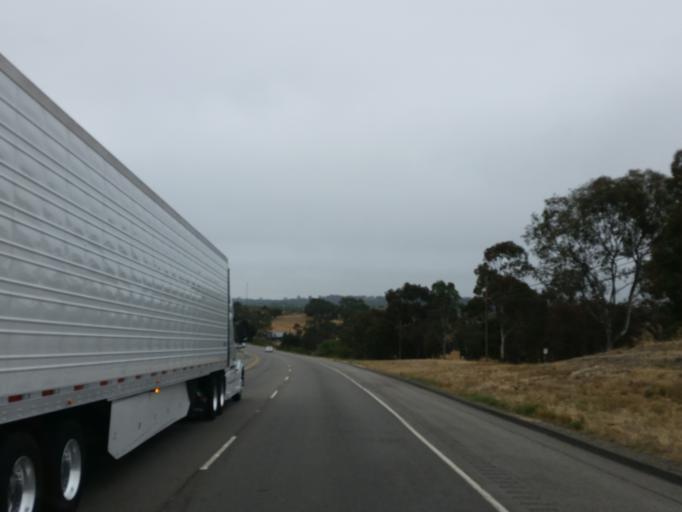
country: US
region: California
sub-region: San Luis Obispo County
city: Arroyo Grande
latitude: 35.0935
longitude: -120.5437
